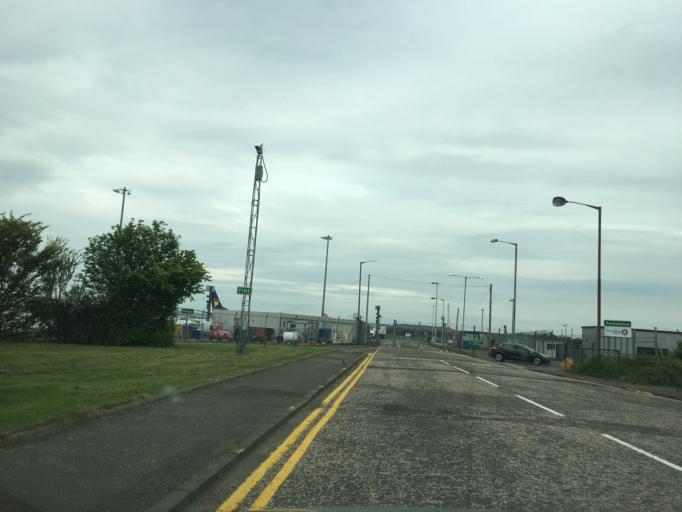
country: GB
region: Scotland
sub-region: Edinburgh
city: Ratho
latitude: 55.9525
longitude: -3.3530
